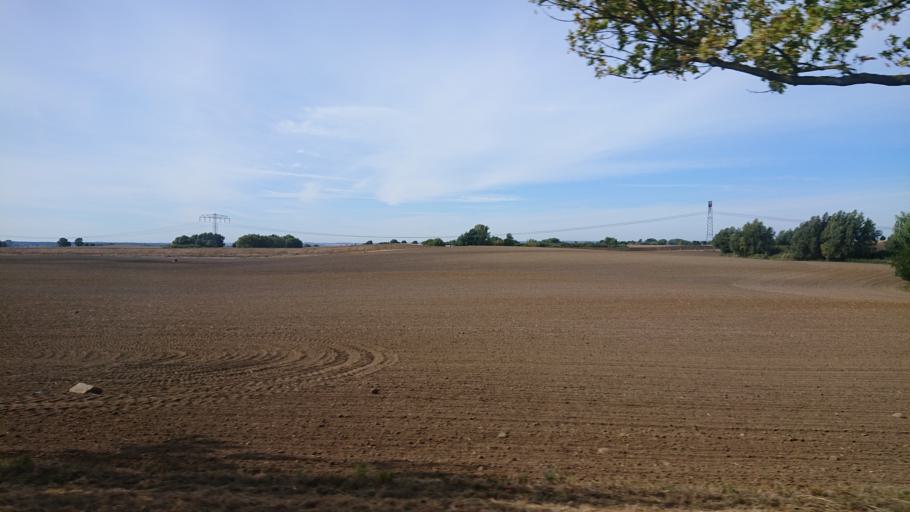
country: DE
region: Brandenburg
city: Gramzow
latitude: 53.2477
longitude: 13.9657
